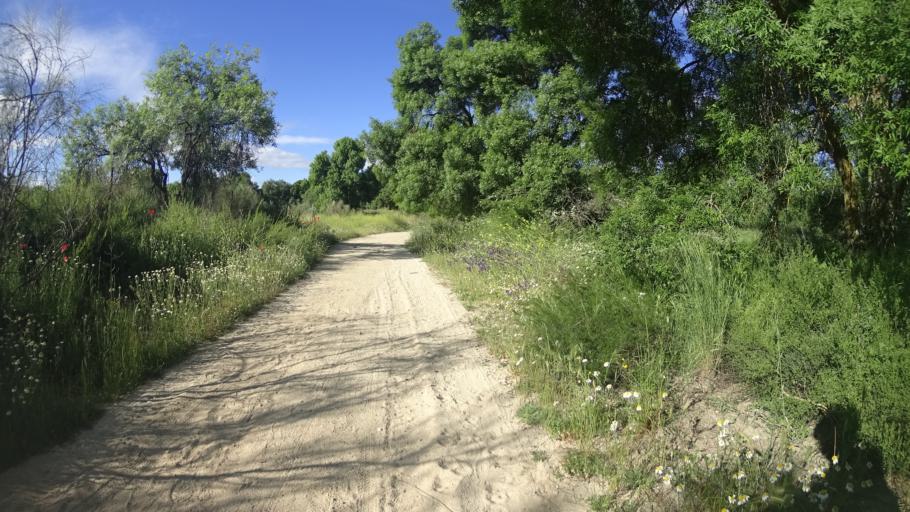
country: ES
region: Madrid
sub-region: Provincia de Madrid
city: Villanueva del Pardillo
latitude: 40.5096
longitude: -3.9392
